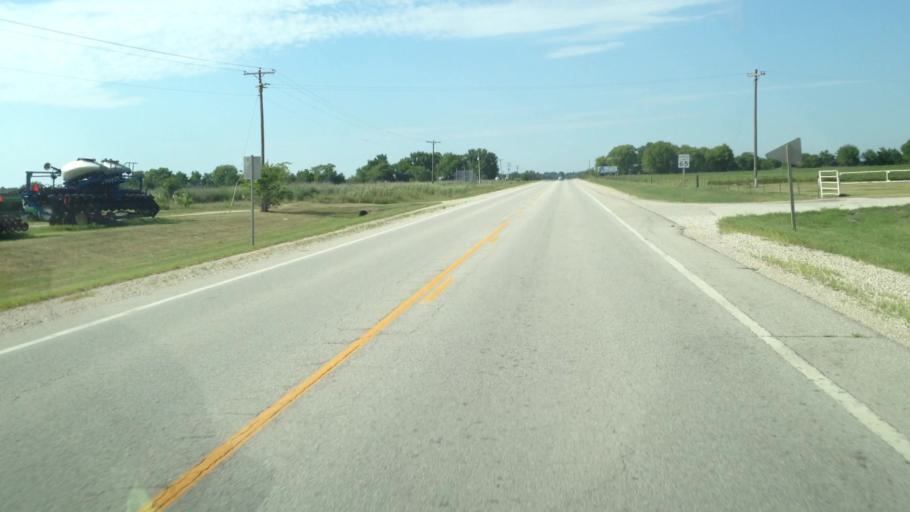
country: US
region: Kansas
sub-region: Neosho County
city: Erie
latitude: 37.5186
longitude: -95.2700
